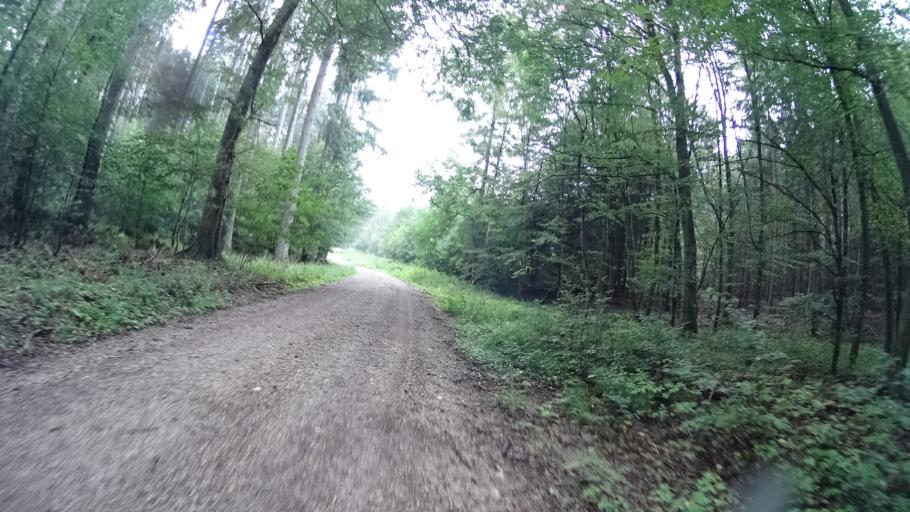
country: DE
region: Bavaria
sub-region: Upper Bavaria
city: Bohmfeld
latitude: 48.9039
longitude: 11.3559
